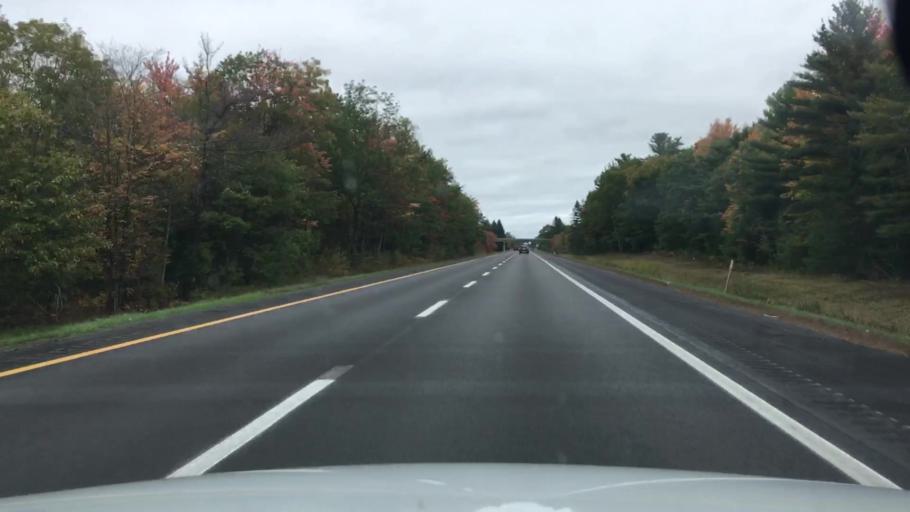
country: US
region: Maine
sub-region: Penobscot County
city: Veazie
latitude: 44.8415
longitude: -68.7339
